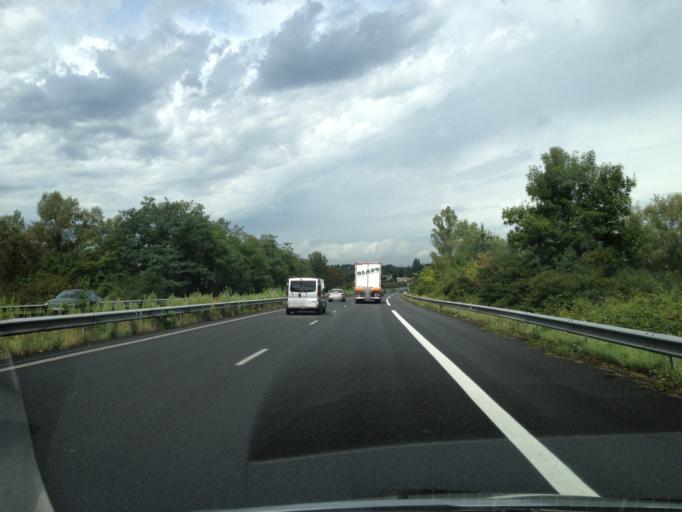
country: FR
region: Aquitaine
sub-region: Departement de la Gironde
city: Langon
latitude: 44.5336
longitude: -0.2490
